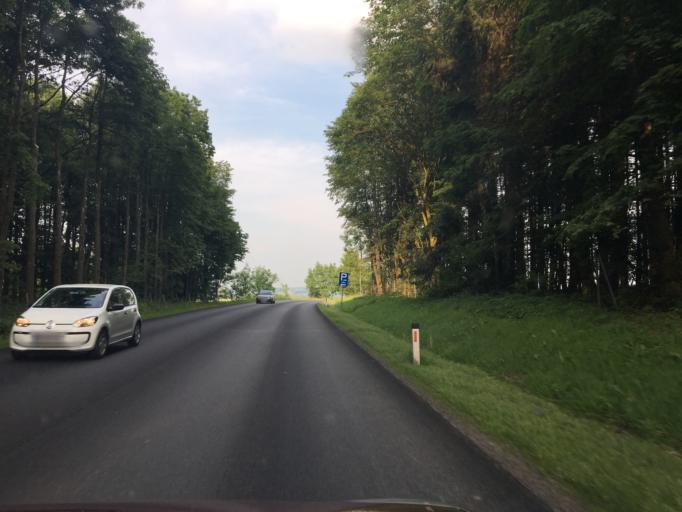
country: AT
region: Upper Austria
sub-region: Politischer Bezirk Vocklabruck
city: Wolfsegg am Hausruck
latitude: 48.1985
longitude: 13.6248
